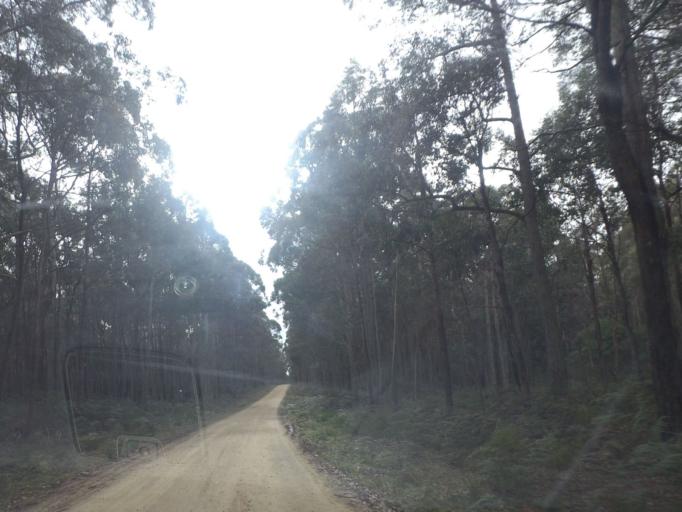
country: AU
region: Victoria
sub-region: Moorabool
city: Bacchus Marsh
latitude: -37.4204
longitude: 144.3092
